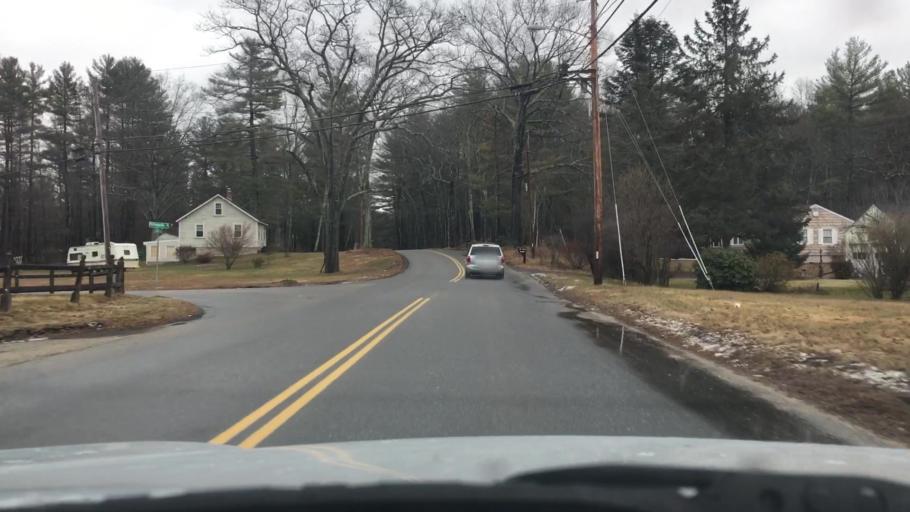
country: US
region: Massachusetts
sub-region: Worcester County
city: Athol
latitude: 42.5712
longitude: -72.2633
